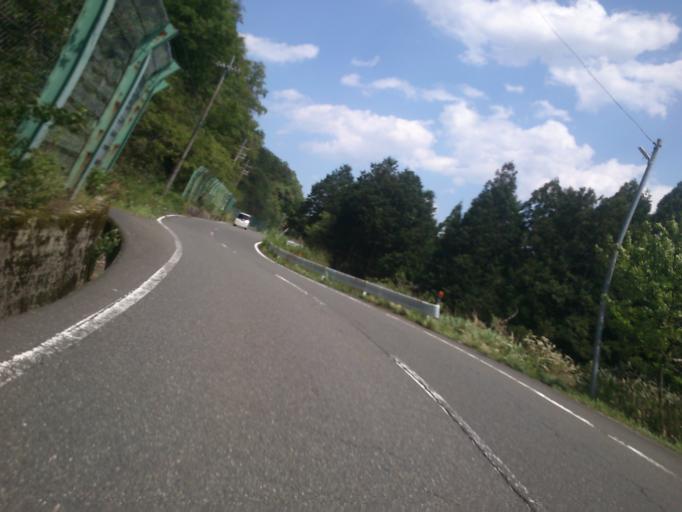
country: JP
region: Kyoto
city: Miyazu
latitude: 35.6898
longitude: 135.1197
